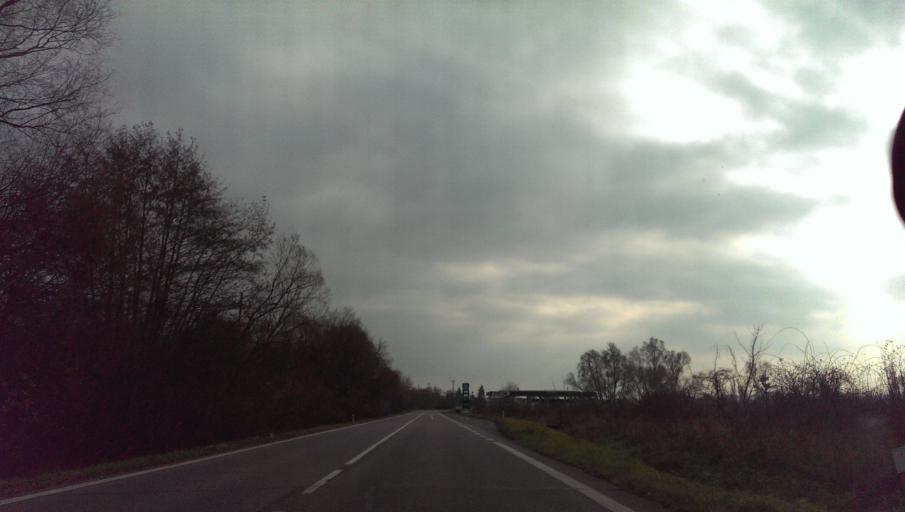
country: CZ
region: Zlin
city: Tlumacov
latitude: 49.2632
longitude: 17.4946
